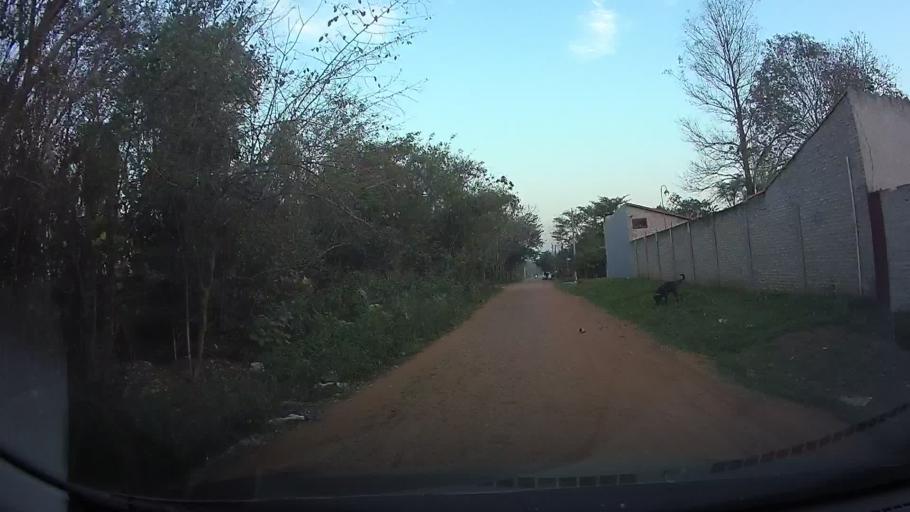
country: PY
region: Central
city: Limpio
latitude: -25.2307
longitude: -57.4691
